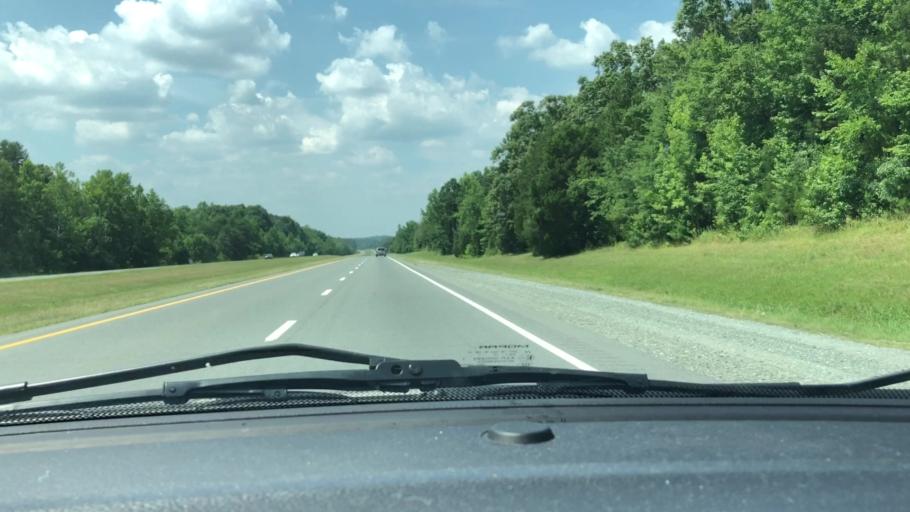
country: US
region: North Carolina
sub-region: Guilford County
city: Forest Oaks
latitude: 35.9344
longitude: -79.6835
